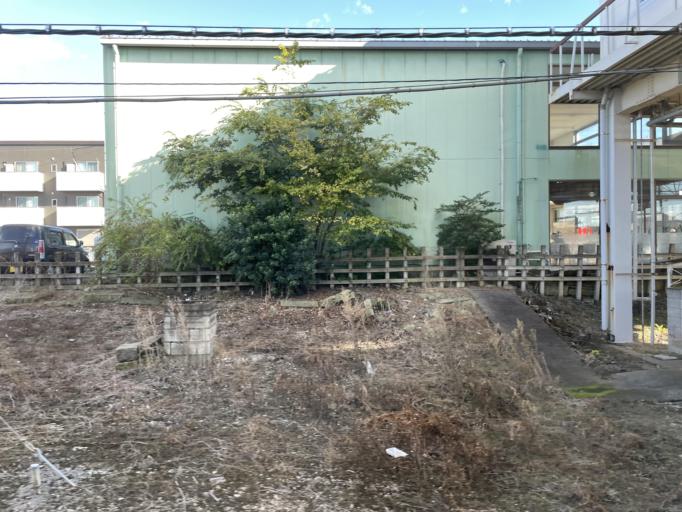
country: JP
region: Tochigi
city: Utsunomiya-shi
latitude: 36.5308
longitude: 139.8609
